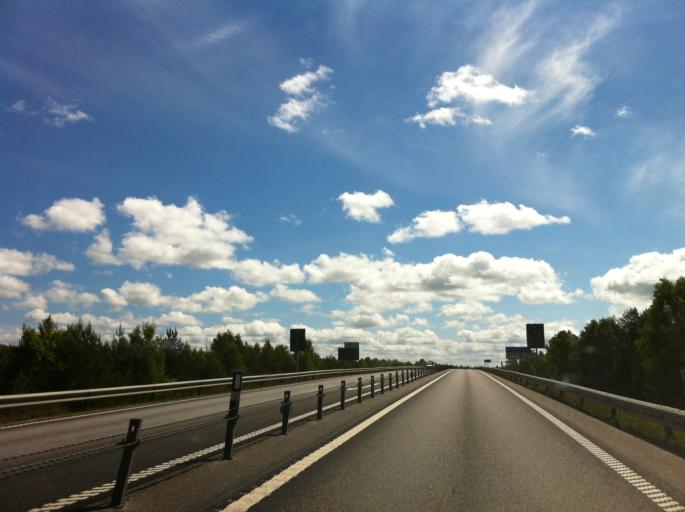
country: SE
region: Vaestra Goetaland
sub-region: Vanersborgs Kommun
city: Vanersborg
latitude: 58.3589
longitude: 12.2584
